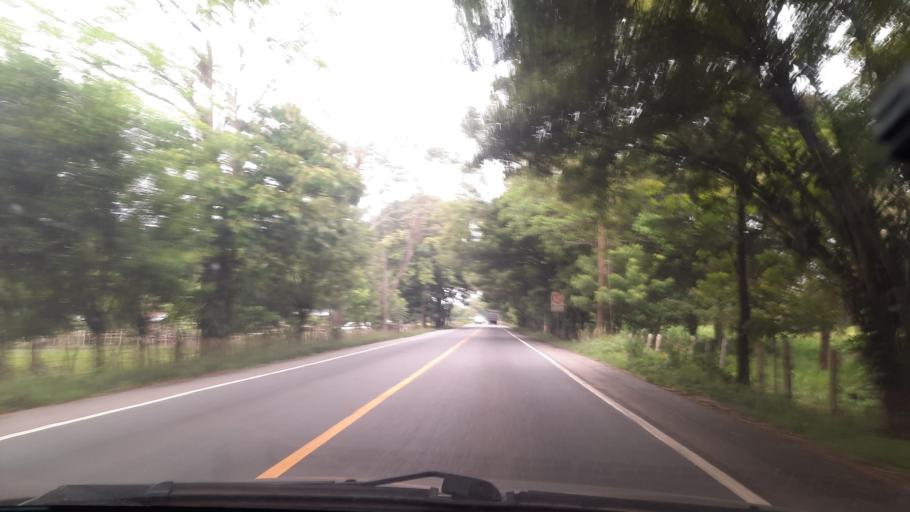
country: GT
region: Izabal
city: Morales
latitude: 15.4582
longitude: -88.9330
